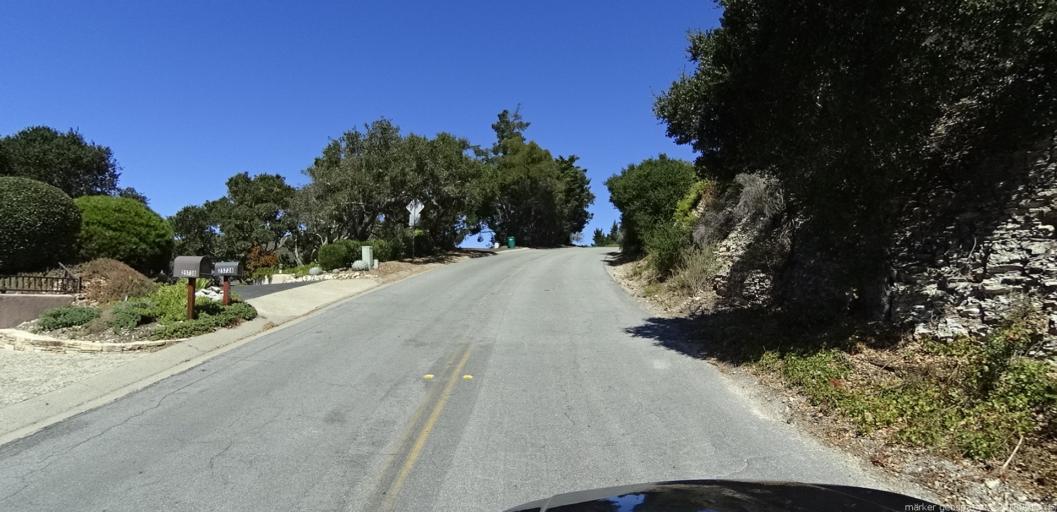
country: US
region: California
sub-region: Monterey County
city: Carmel Valley Village
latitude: 36.5279
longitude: -121.8040
